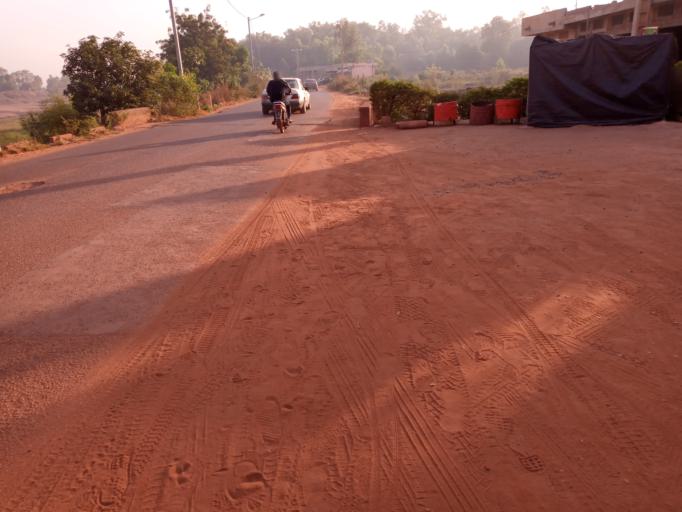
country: ML
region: Bamako
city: Bamako
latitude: 12.6292
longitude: -7.9465
